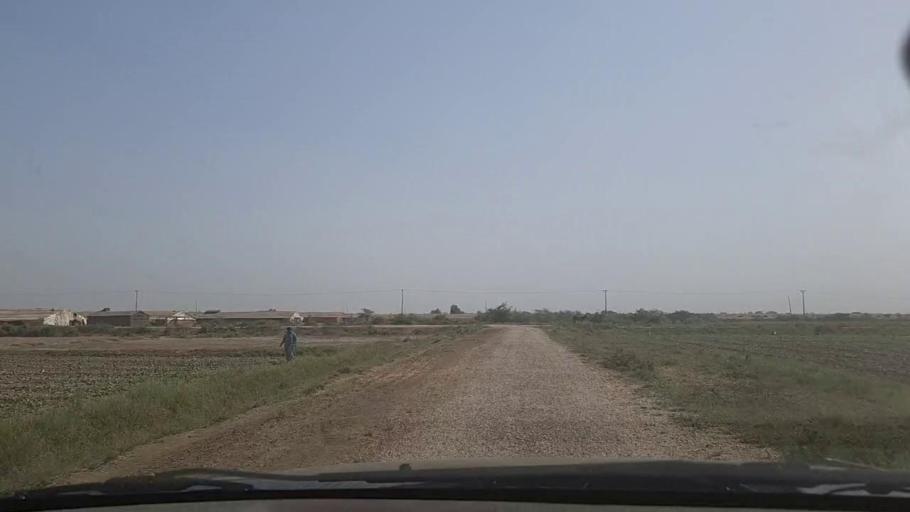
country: PK
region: Sindh
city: Keti Bandar
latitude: 24.1985
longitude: 67.5494
